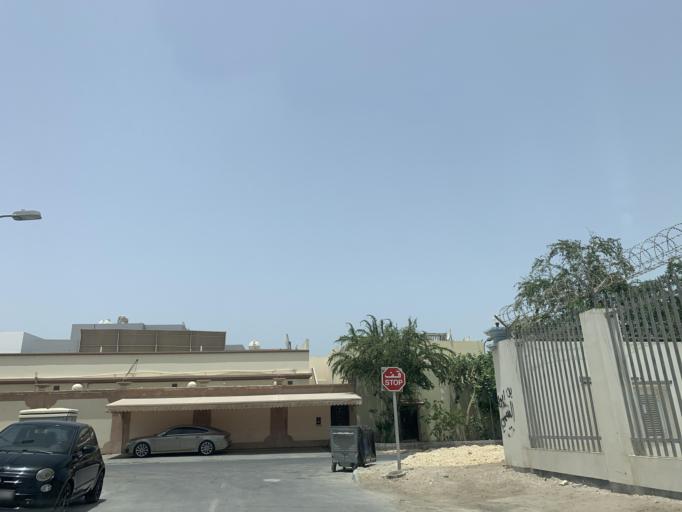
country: BH
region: Northern
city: Sitrah
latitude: 26.1450
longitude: 50.5893
